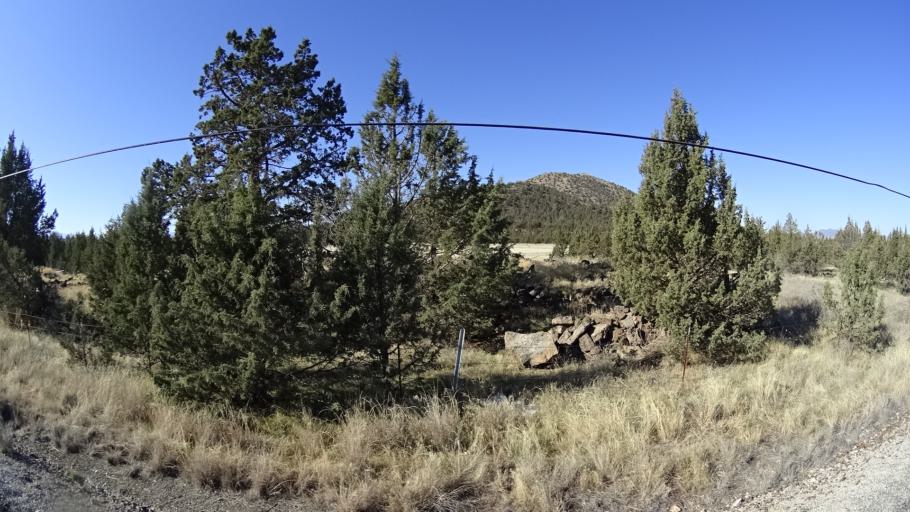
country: US
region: California
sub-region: Siskiyou County
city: Montague
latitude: 41.6682
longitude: -122.3696
